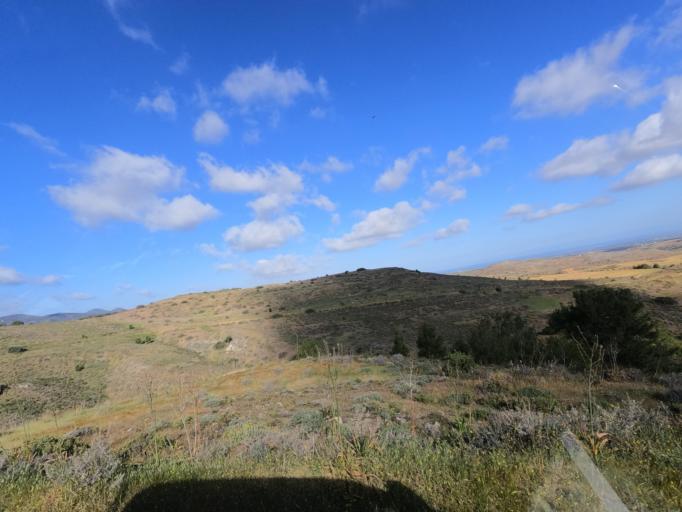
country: CY
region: Lefkosia
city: Peristerona
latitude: 35.0670
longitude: 33.0526
